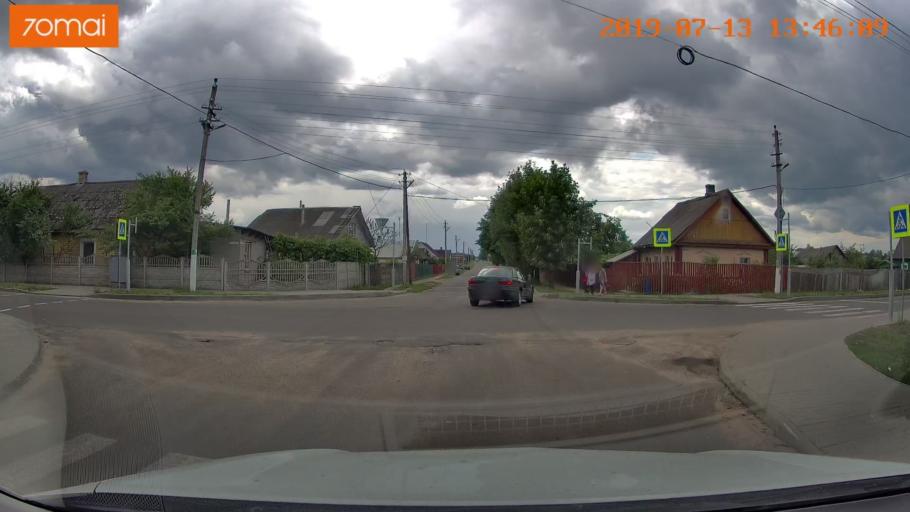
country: BY
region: Mogilev
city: Asipovichy
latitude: 53.2961
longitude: 28.6313
